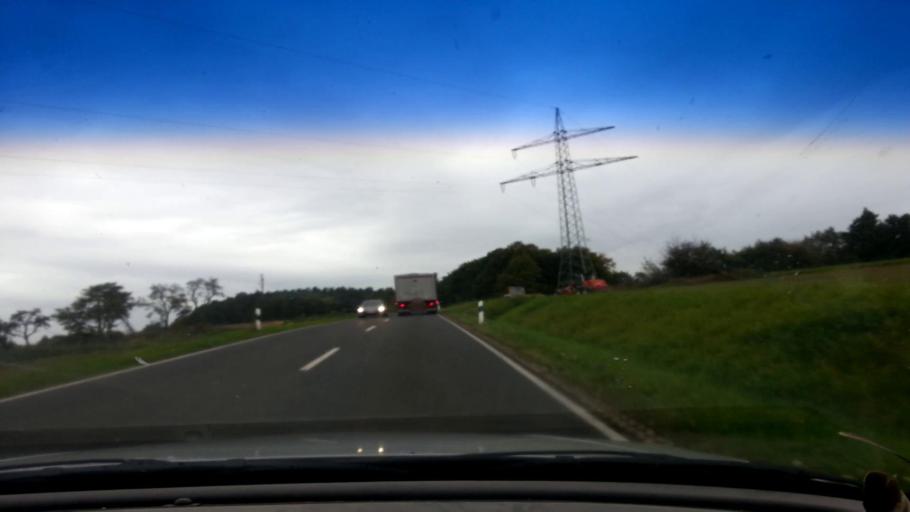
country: DE
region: Bavaria
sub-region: Upper Franconia
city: Priesendorf
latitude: 49.9027
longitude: 10.7031
